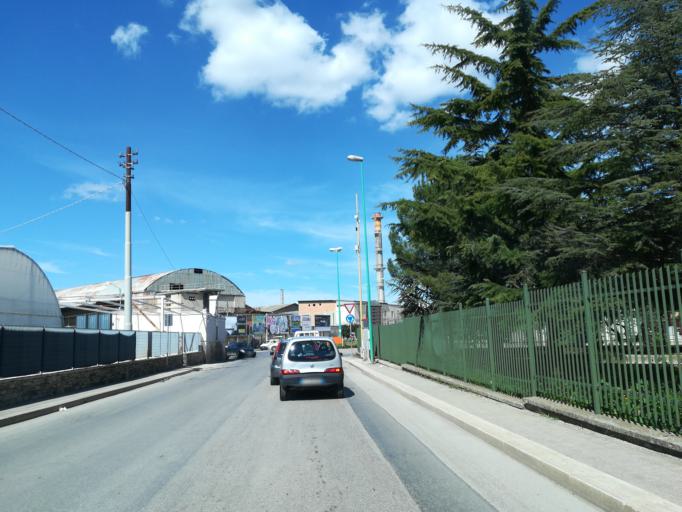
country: IT
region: Apulia
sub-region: Provincia di Bari
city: Terlizzi
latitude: 41.1243
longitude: 16.5476
